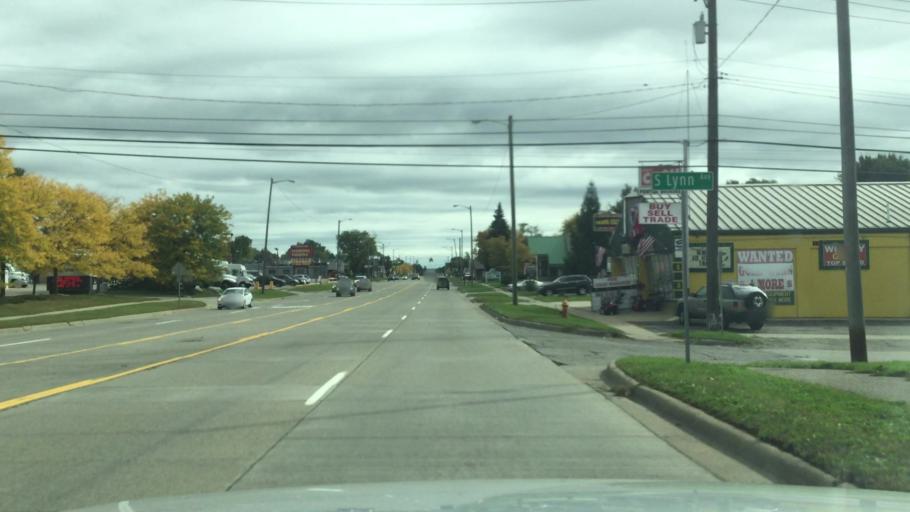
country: US
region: Michigan
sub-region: Oakland County
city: Sylvan Lake
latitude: 42.6348
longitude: -83.3358
